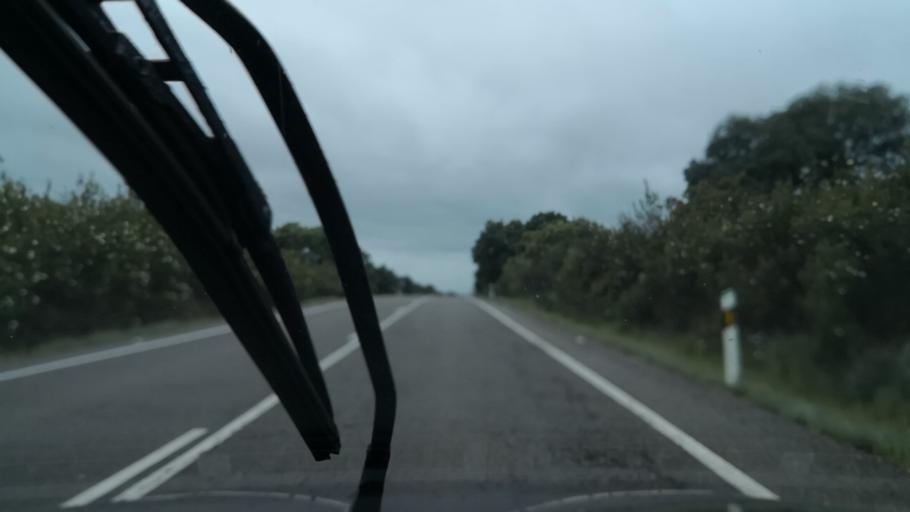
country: ES
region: Extremadura
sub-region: Provincia de Badajoz
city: Puebla de Obando
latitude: 39.1539
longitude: -6.6467
